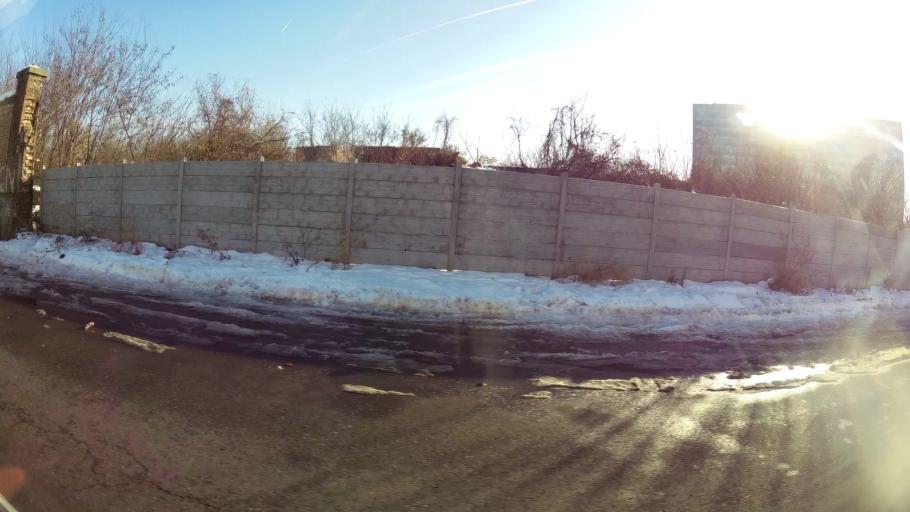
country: RO
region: Bucuresti
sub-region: Municipiul Bucuresti
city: Bucuresti
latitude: 44.4208
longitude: 26.0810
